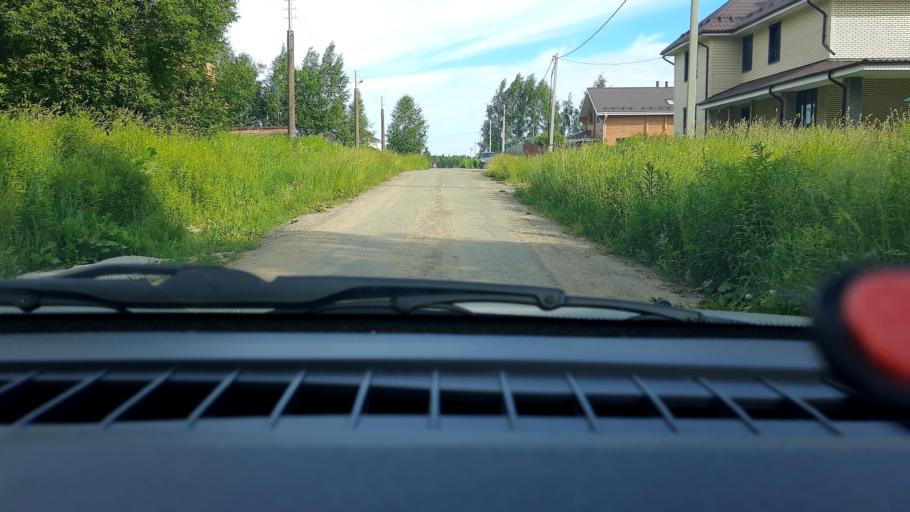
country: RU
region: Nizjnij Novgorod
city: Afonino
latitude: 56.2477
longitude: 44.0709
